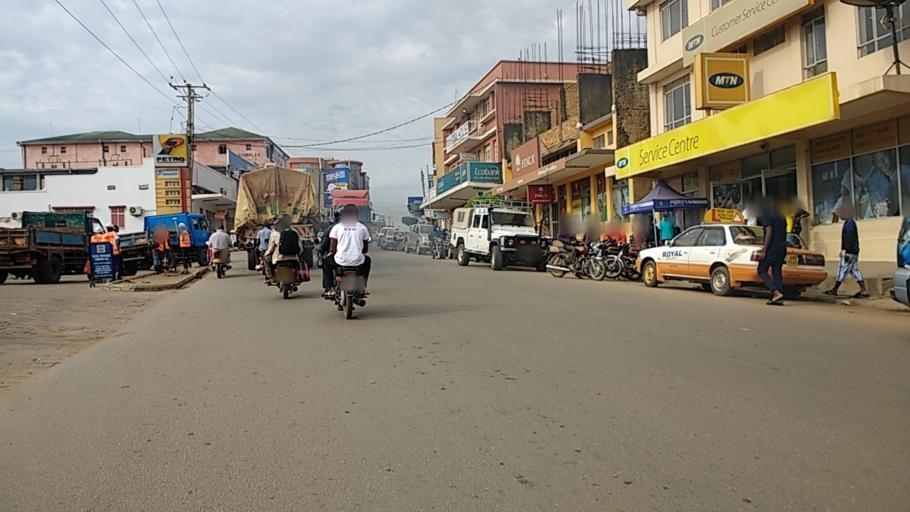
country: UG
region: Western Region
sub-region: Mbarara District
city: Mbarara
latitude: -0.6035
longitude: 30.6630
